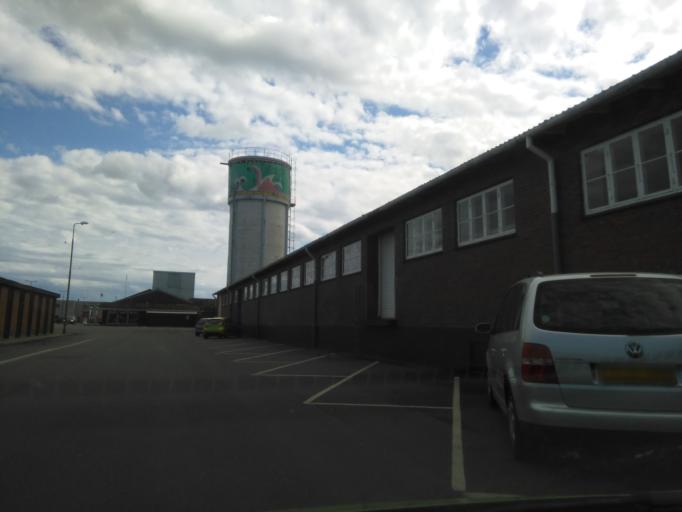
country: DK
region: Capital Region
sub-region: Bornholm Kommune
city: Nexo
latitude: 55.0620
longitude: 15.1346
